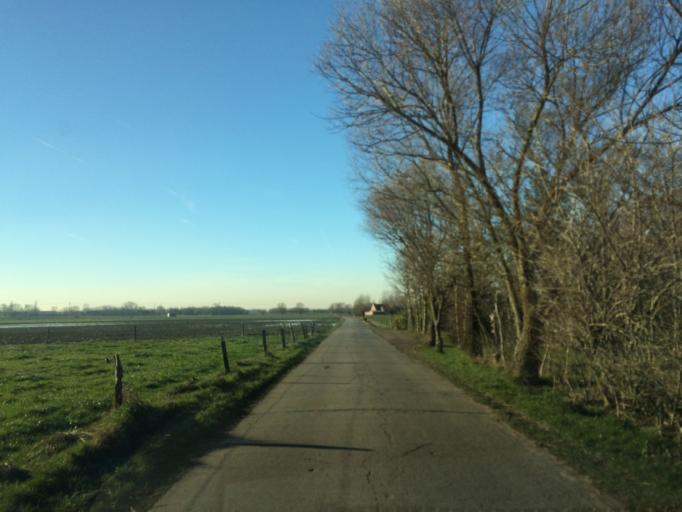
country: BE
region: Flanders
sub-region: Provincie West-Vlaanderen
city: Jabbeke
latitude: 51.1482
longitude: 3.0545
